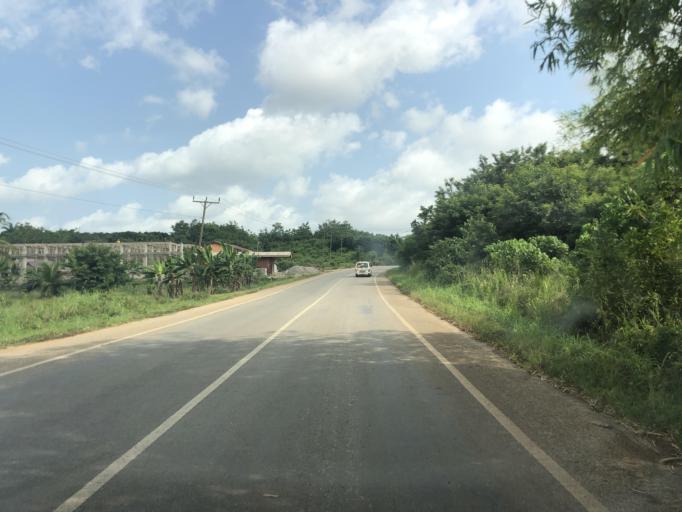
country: GH
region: Central
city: Cape Coast
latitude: 5.1905
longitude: -1.3143
